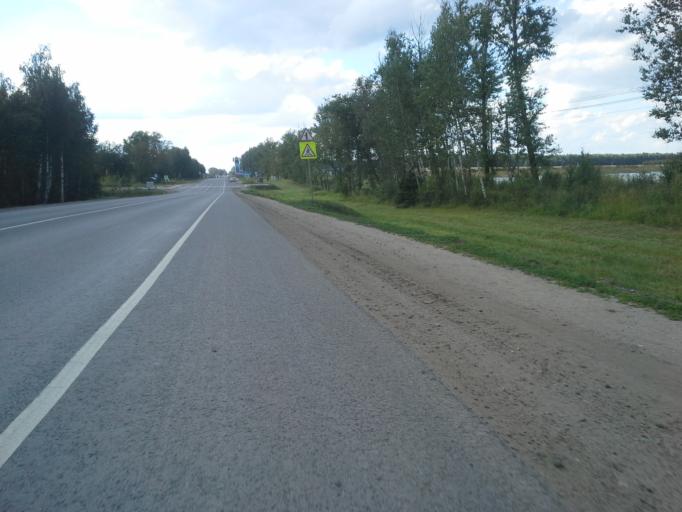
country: RU
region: Moskovskaya
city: L'vovskiy
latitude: 55.3415
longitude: 37.4617
